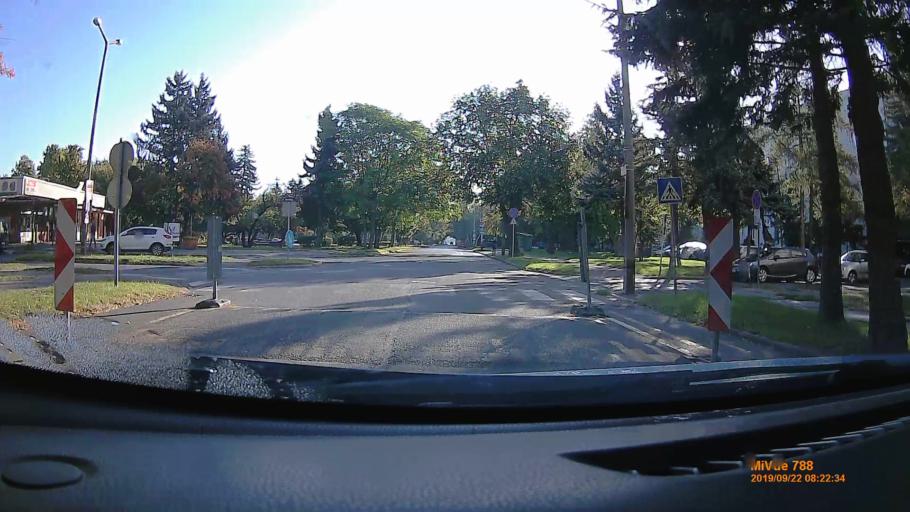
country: HU
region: Borsod-Abauj-Zemplen
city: Sajobabony
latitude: 48.0972
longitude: 20.7044
